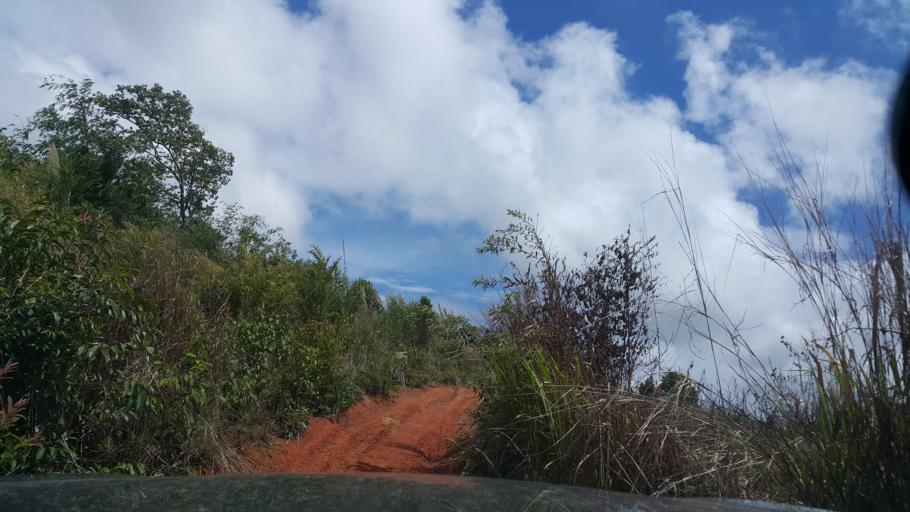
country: TH
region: Loei
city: Na Haeo
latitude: 17.5947
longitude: 100.8903
